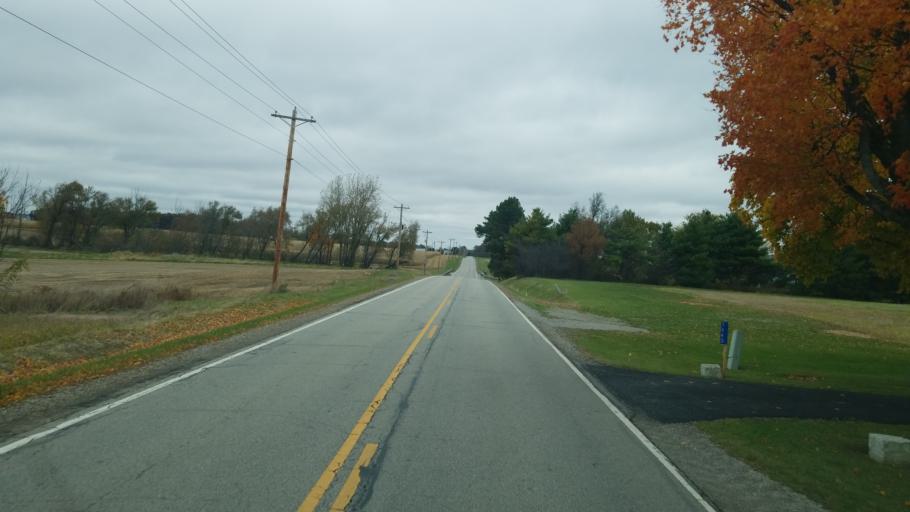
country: US
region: Ohio
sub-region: Huron County
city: Willard
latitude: 40.9841
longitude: -82.8533
